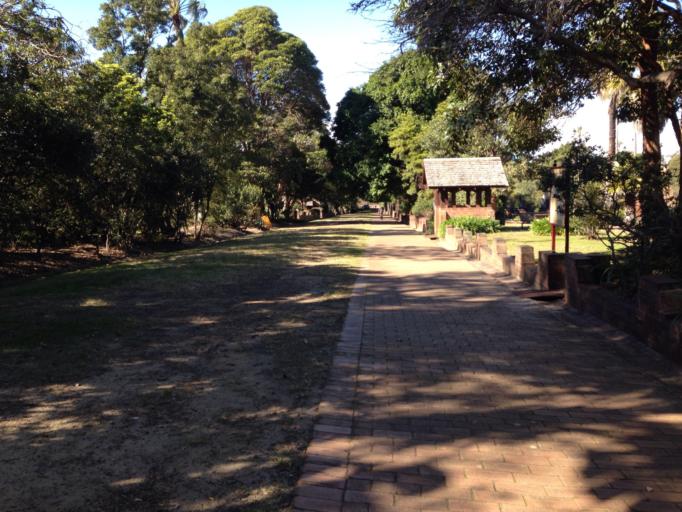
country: AU
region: New South Wales
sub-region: Willoughby
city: Artarmon
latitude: -33.8223
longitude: 151.1876
